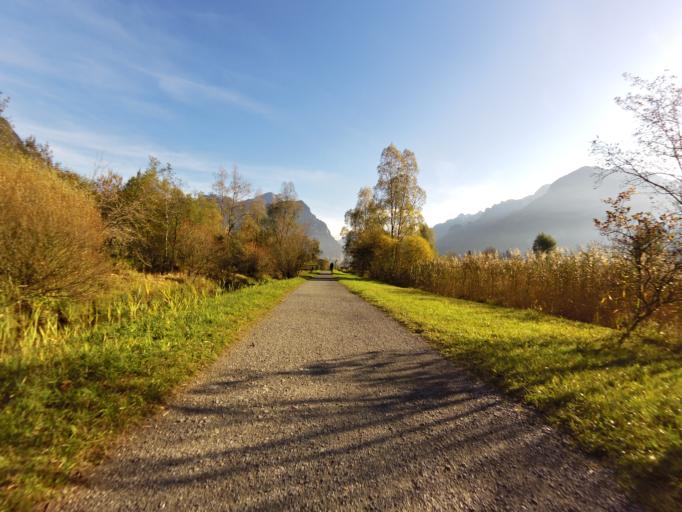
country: CH
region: Uri
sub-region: Uri
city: Flueelen
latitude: 46.8981
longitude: 8.6187
